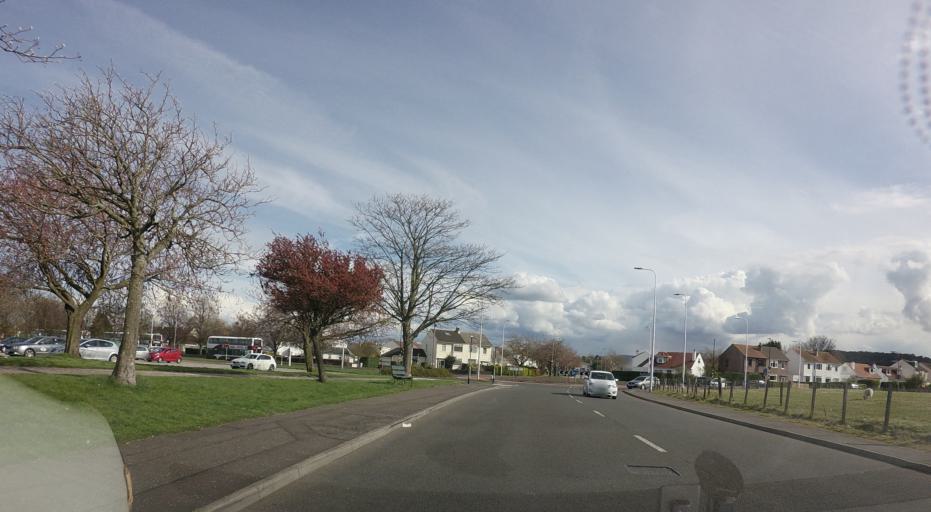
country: GB
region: Scotland
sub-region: Edinburgh
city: Colinton
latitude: 55.9725
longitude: -3.2729
